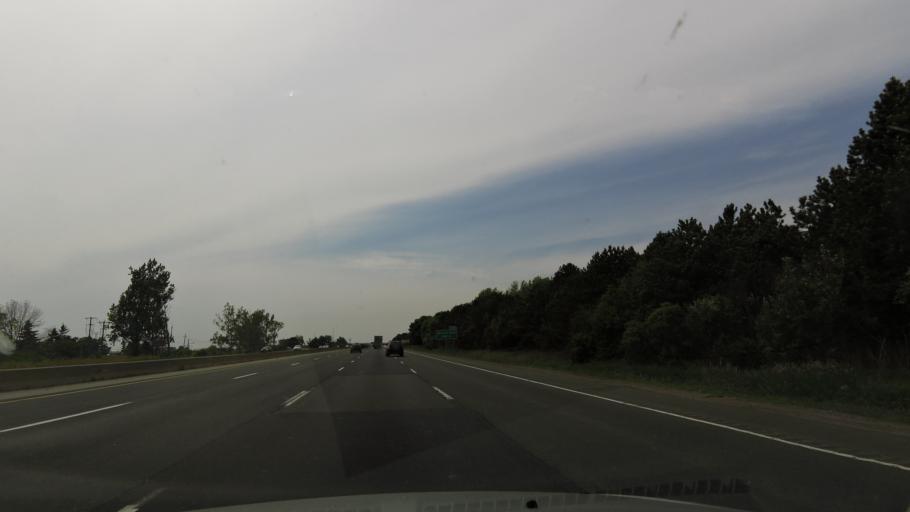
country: CA
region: Ontario
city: Oshawa
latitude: 43.9022
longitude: -78.6367
